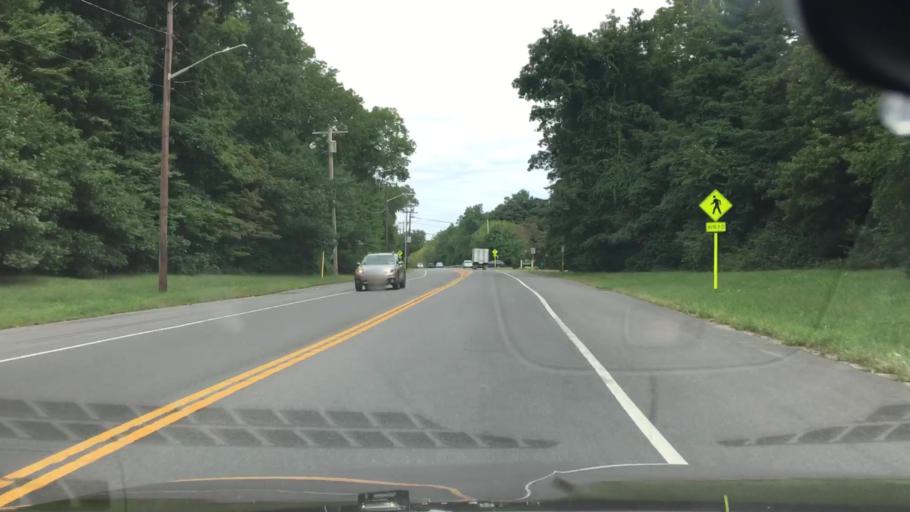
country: US
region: New York
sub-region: Suffolk County
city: Village of the Branch
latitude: 40.8476
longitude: -73.1888
